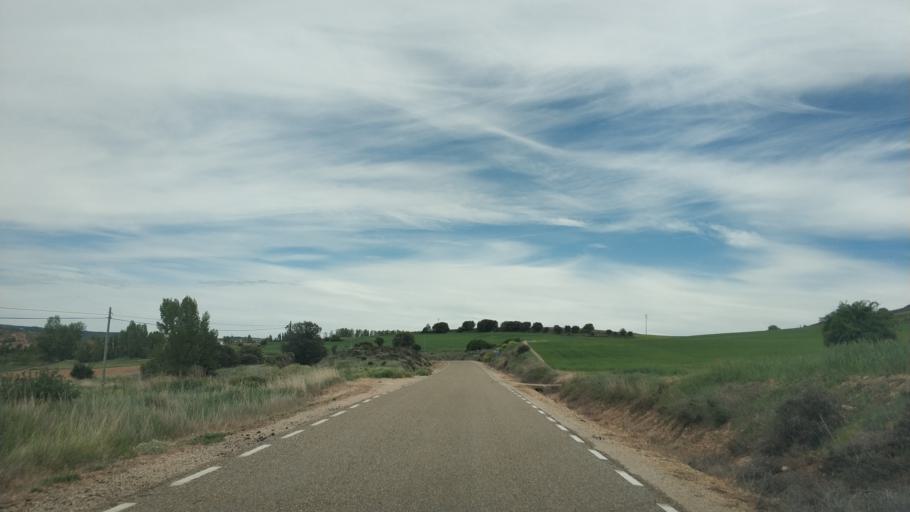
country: ES
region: Castille and Leon
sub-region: Provincia de Soria
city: Berlanga de Duero
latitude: 41.4432
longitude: -2.8281
